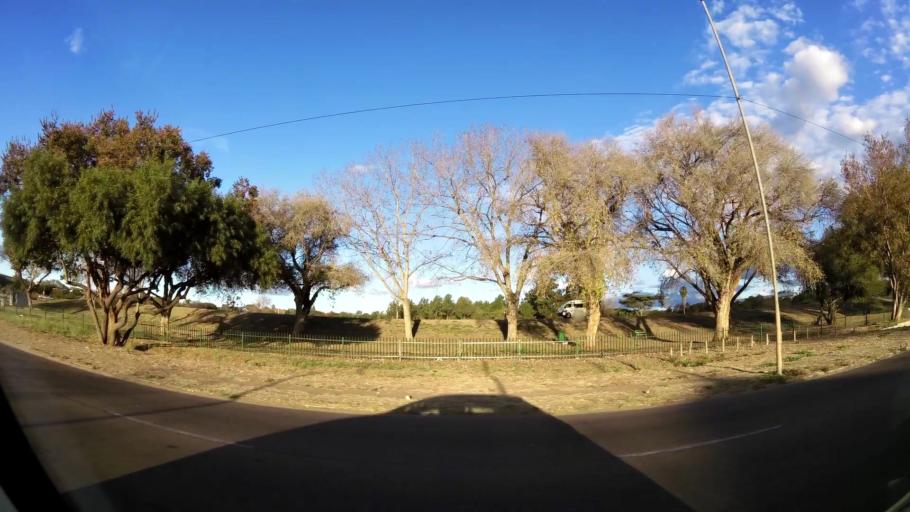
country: ZA
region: Limpopo
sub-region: Capricorn District Municipality
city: Polokwane
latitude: -23.8861
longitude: 29.4563
